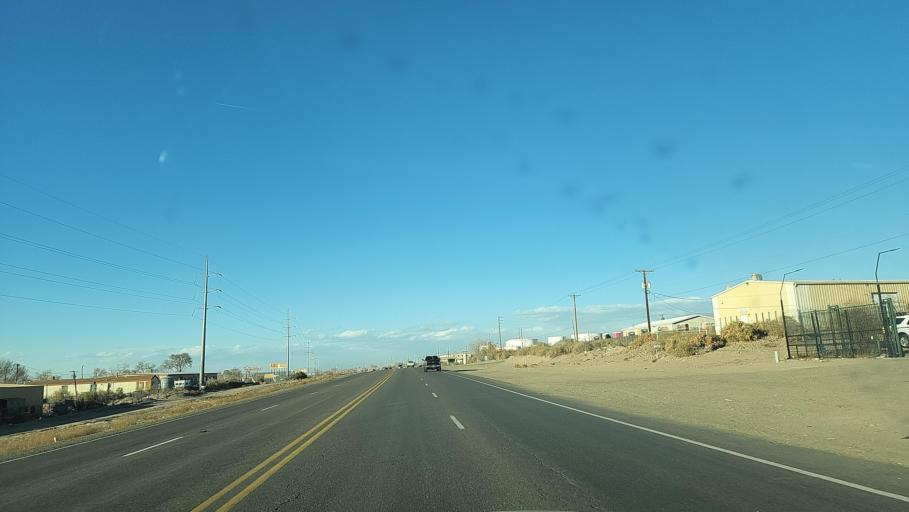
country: US
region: New Mexico
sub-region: Bernalillo County
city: South Valley
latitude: 35.0167
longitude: -106.6477
